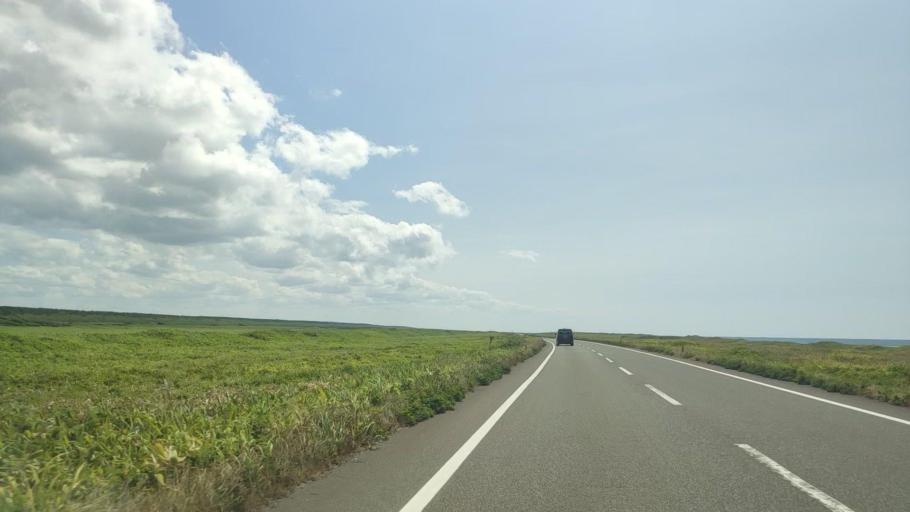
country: JP
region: Hokkaido
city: Wakkanai
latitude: 45.1629
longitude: 141.5849
